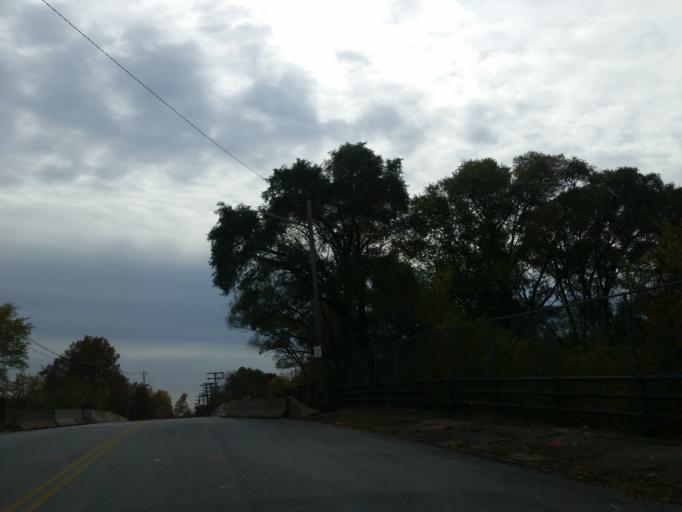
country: US
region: Ohio
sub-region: Cuyahoga County
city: Newburgh Heights
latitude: 41.4863
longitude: -81.6364
